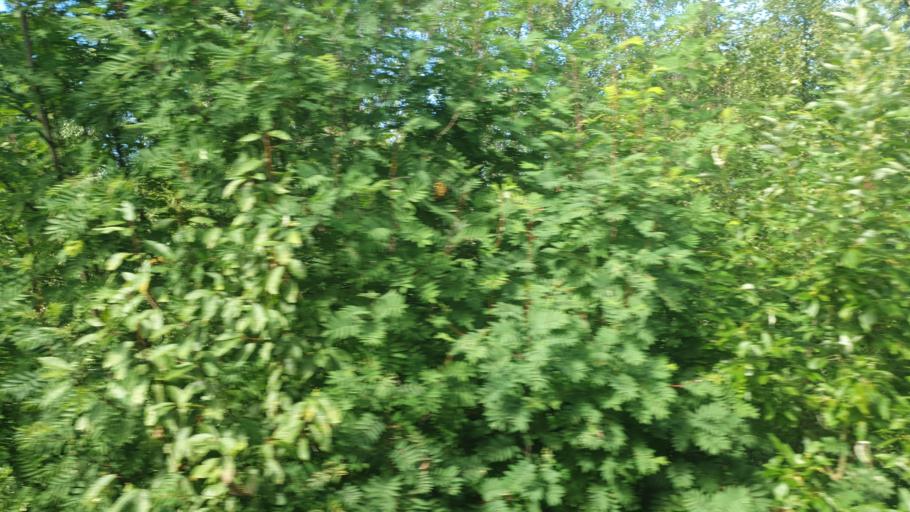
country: NO
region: Sor-Trondelag
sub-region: Orkdal
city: Orkanger
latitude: 63.2712
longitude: 9.8197
